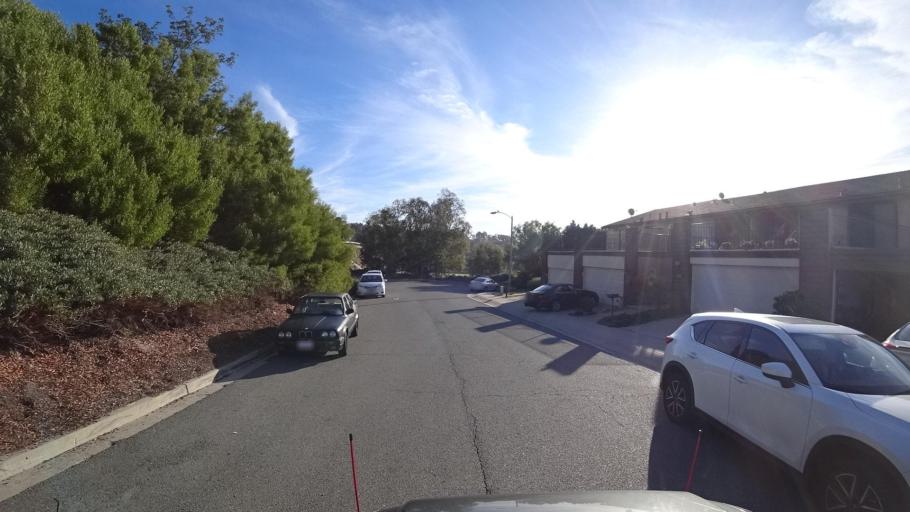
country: US
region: California
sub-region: San Diego County
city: Spring Valley
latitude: 32.7350
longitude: -116.9760
